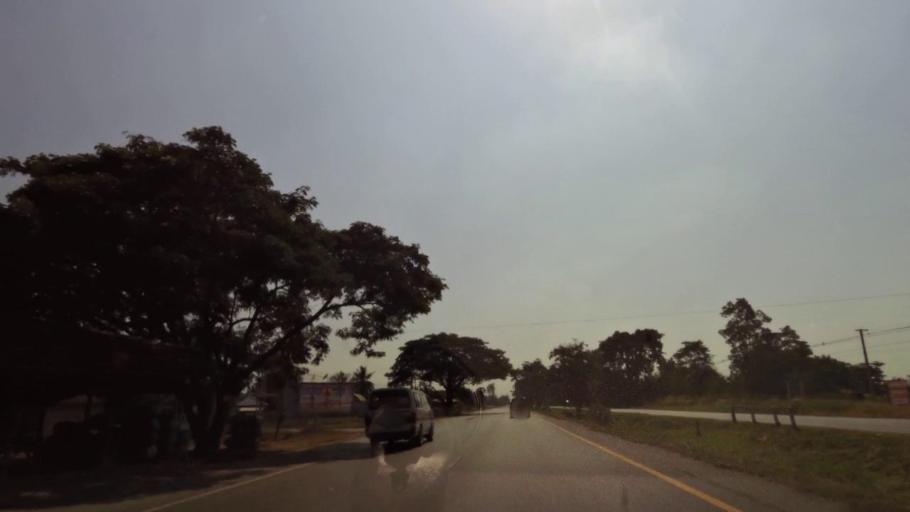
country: TH
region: Phichit
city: Bueng Na Rang
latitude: 16.3376
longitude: 100.1284
